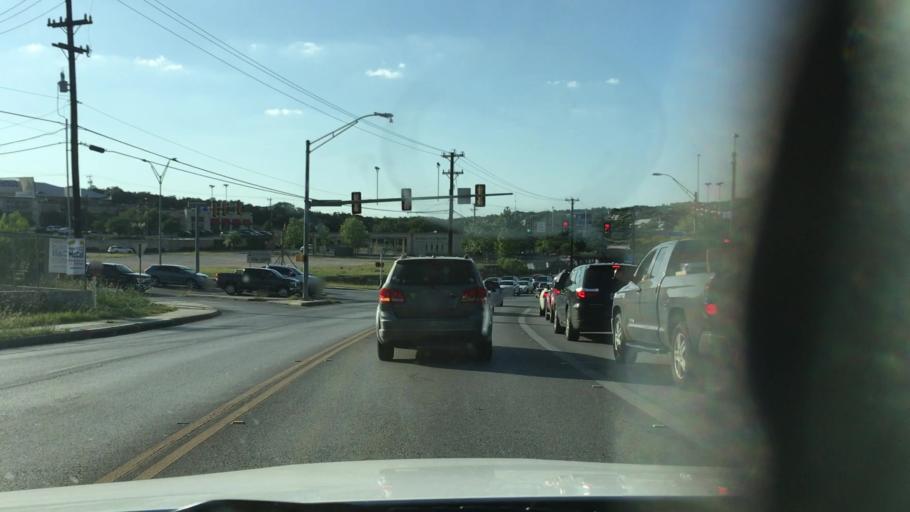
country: US
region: Texas
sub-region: Bexar County
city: Timberwood Park
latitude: 29.6605
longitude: -98.4346
